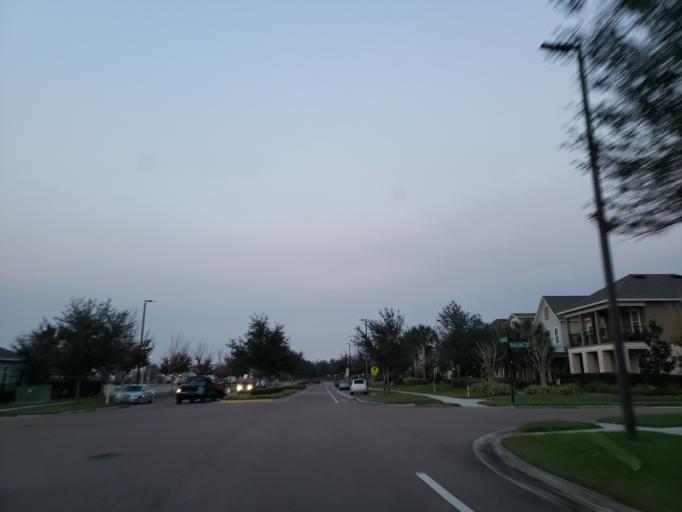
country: US
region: Florida
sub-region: Hillsborough County
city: Boyette
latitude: 27.8458
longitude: -82.2561
